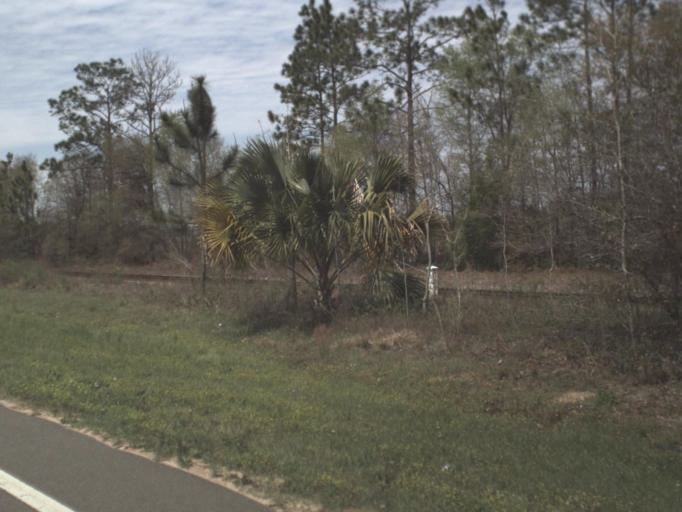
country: US
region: Florida
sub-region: Okaloosa County
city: Crestview
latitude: 30.7045
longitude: -86.7775
